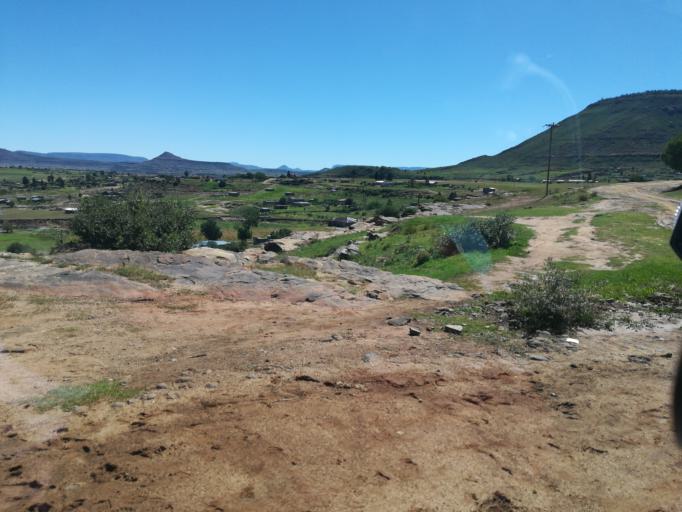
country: LS
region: Mohale's Hoek District
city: Mohale's Hoek
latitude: -30.1069
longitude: 27.4776
